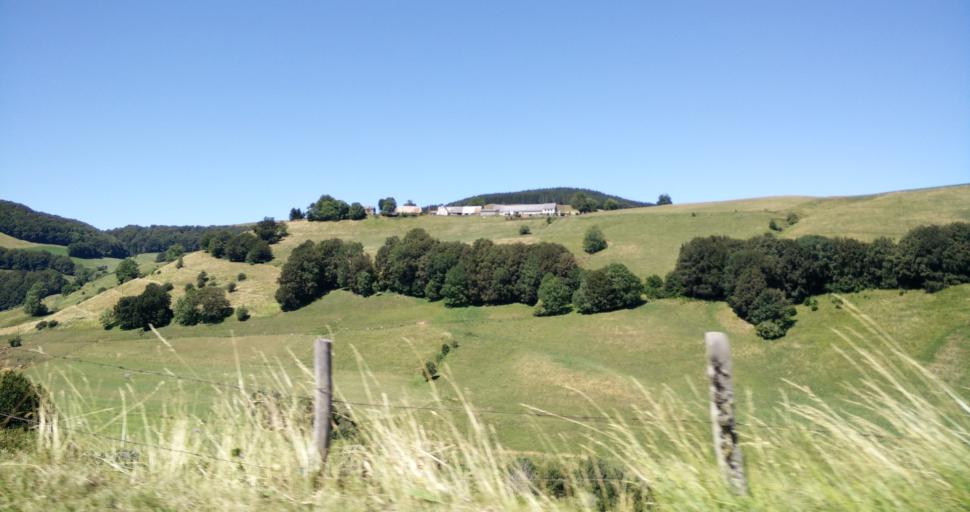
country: FR
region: Auvergne
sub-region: Departement du Puy-de-Dome
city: Mont-Dore
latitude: 45.4842
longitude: 2.9285
